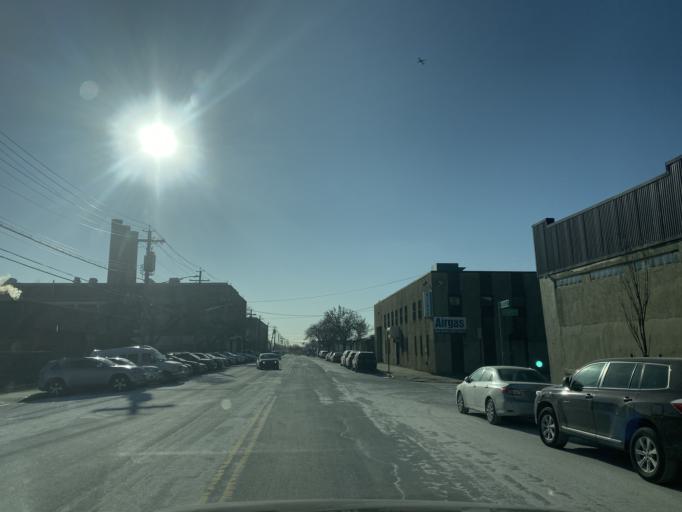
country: US
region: New York
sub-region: Bronx
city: The Bronx
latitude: 40.8266
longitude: -73.8435
